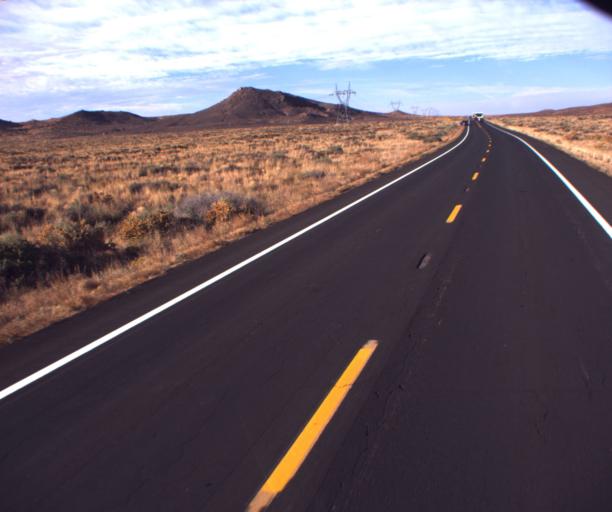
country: US
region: Arizona
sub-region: Apache County
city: Lukachukai
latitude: 36.9630
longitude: -109.4828
